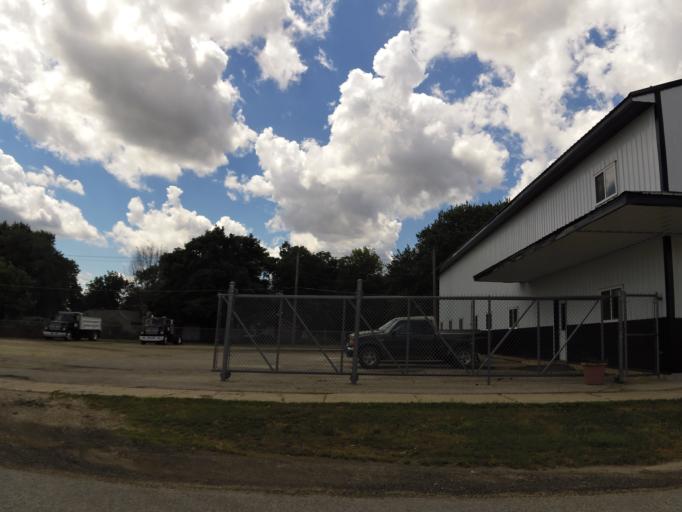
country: US
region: Iowa
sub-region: Fayette County
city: Oelwein
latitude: 42.6167
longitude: -91.9056
